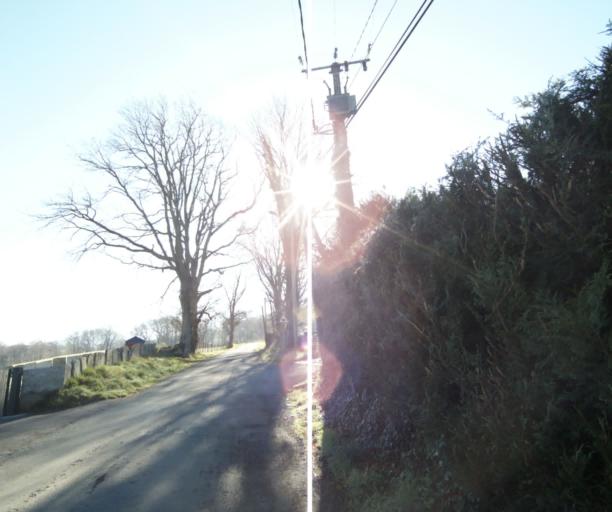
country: FR
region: Aquitaine
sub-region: Departement des Pyrenees-Atlantiques
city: Ascain
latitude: 43.3397
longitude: -1.6444
